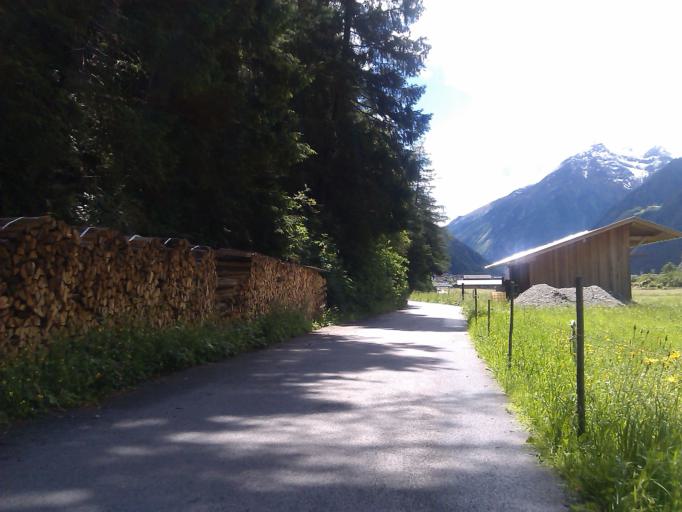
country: AT
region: Tyrol
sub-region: Politischer Bezirk Landeck
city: Pfunds
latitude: 46.9764
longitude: 10.5560
